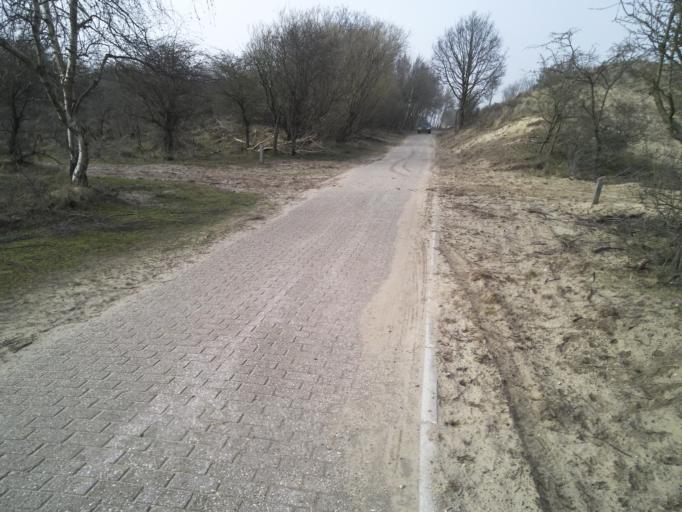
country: NL
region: North Holland
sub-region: Gemeente Zandvoort
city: Zandvoort
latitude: 52.3234
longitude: 4.5396
